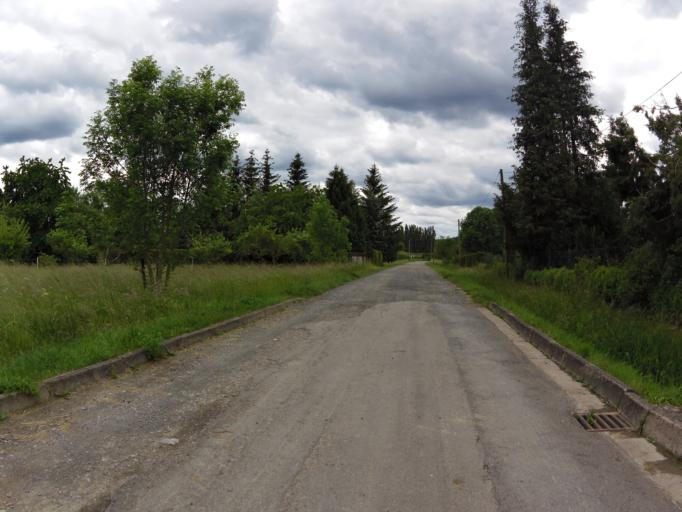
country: DE
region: Thuringia
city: Oberdorla
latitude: 51.1643
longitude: 10.4139
